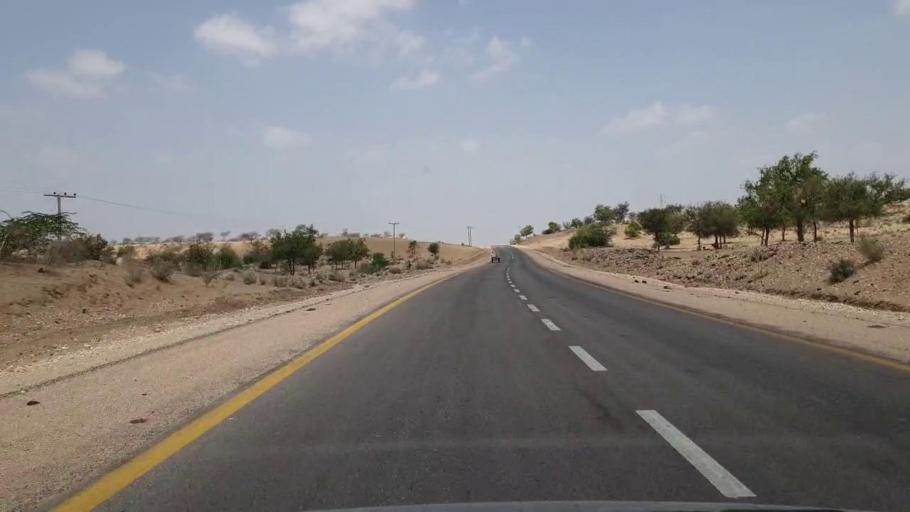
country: PK
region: Sindh
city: Mithi
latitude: 24.7992
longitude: 69.7396
